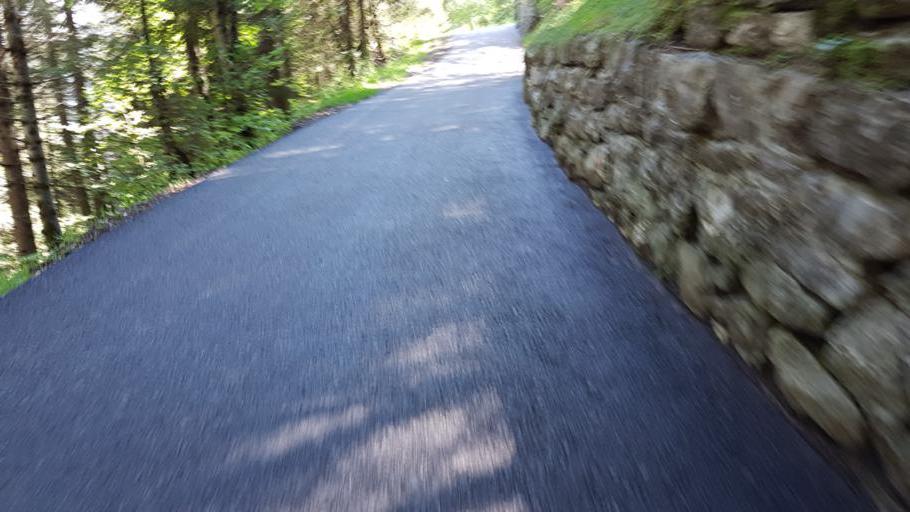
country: CH
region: Bern
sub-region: Frutigen-Niedersimmental District
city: Adelboden
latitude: 46.4856
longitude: 7.5546
